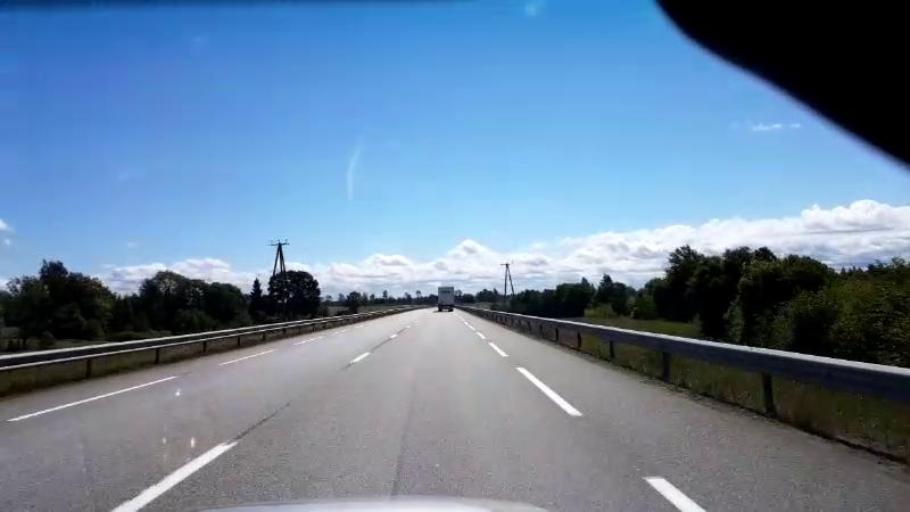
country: LV
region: Saulkrastu
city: Saulkrasti
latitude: 57.3377
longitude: 24.4515
